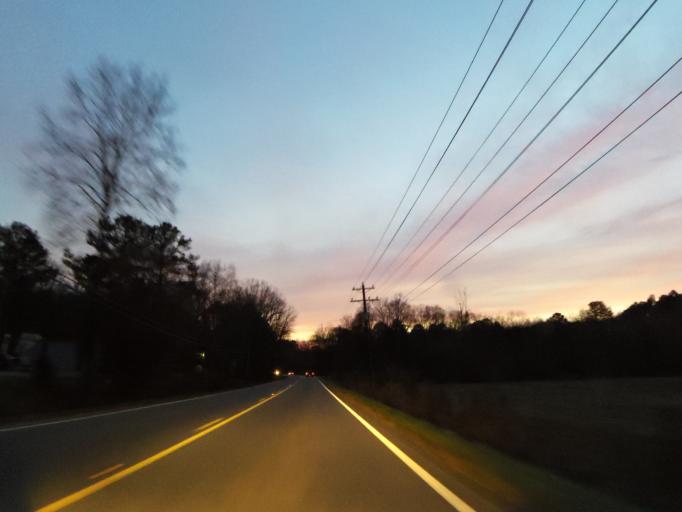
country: US
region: Tennessee
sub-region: Polk County
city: Benton
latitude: 35.1118
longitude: -84.7260
